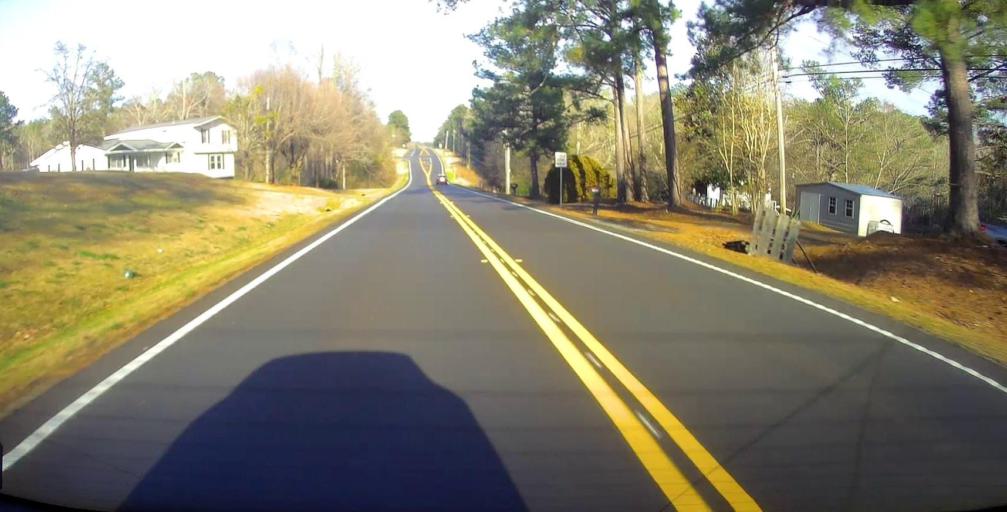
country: US
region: Georgia
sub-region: Harris County
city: Hamilton
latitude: 32.7547
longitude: -84.8942
